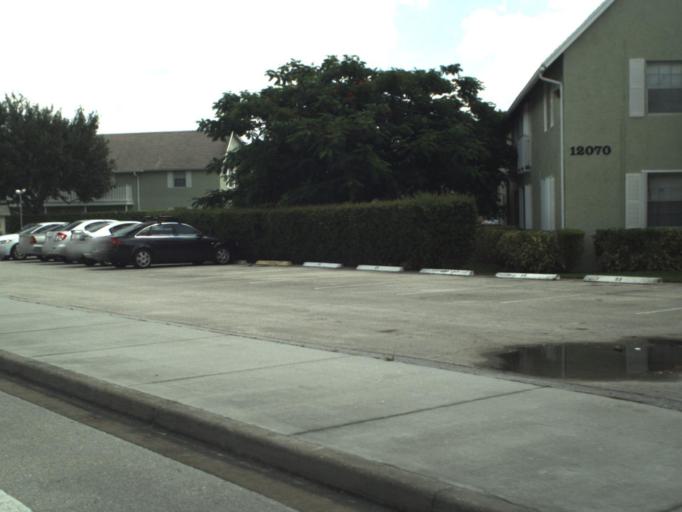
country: US
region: Florida
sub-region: Palm Beach County
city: North Palm Beach
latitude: 26.8543
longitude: -80.0961
